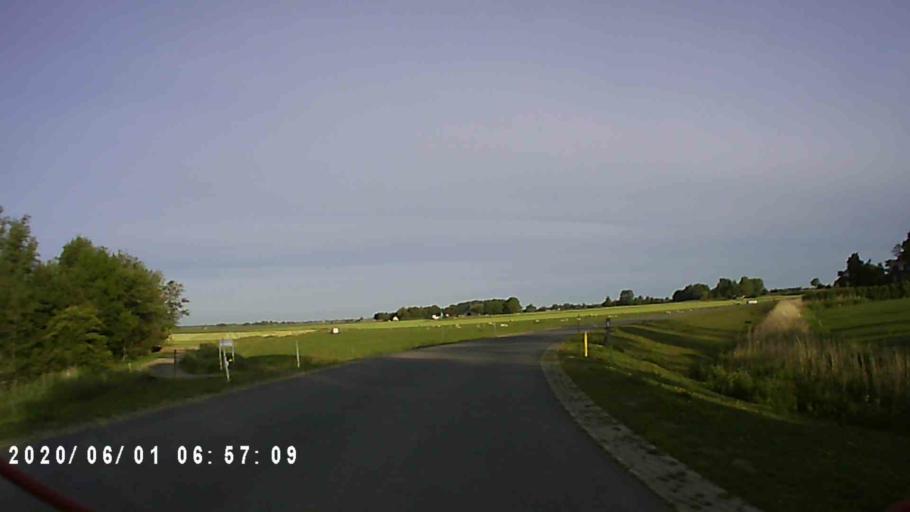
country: NL
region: Friesland
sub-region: Gemeente Kollumerland en Nieuwkruisland
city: Kollum
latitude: 53.3165
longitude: 6.1075
